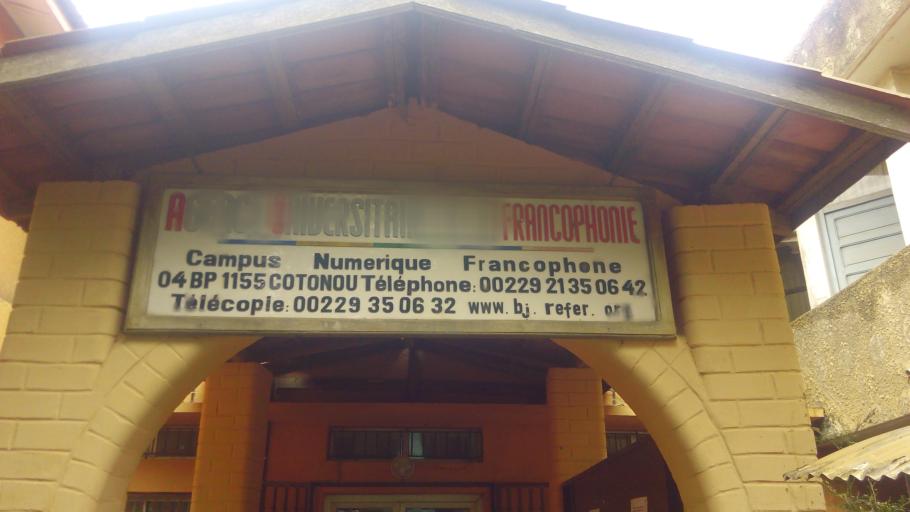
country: BJ
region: Atlantique
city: Abomey-Calavi
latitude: 6.4144
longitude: 2.3430
